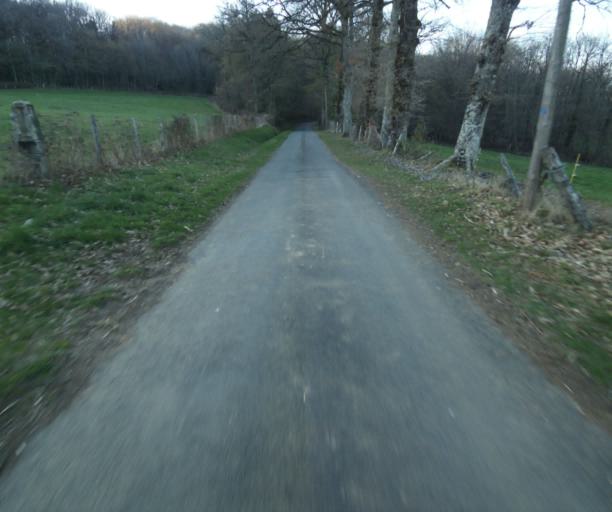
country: FR
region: Limousin
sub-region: Departement de la Correze
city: Seilhac
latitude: 45.3472
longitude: 1.7207
